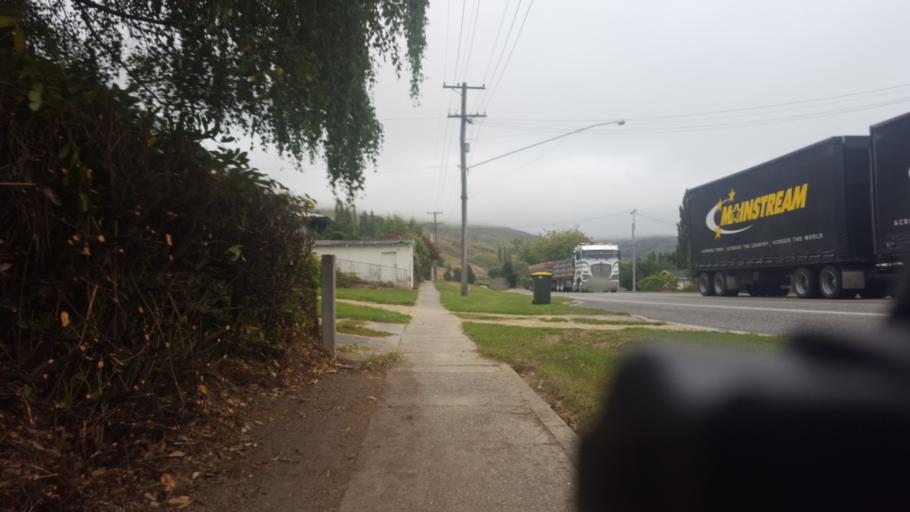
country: NZ
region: Otago
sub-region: Queenstown-Lakes District
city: Kingston
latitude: -45.5355
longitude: 169.3048
